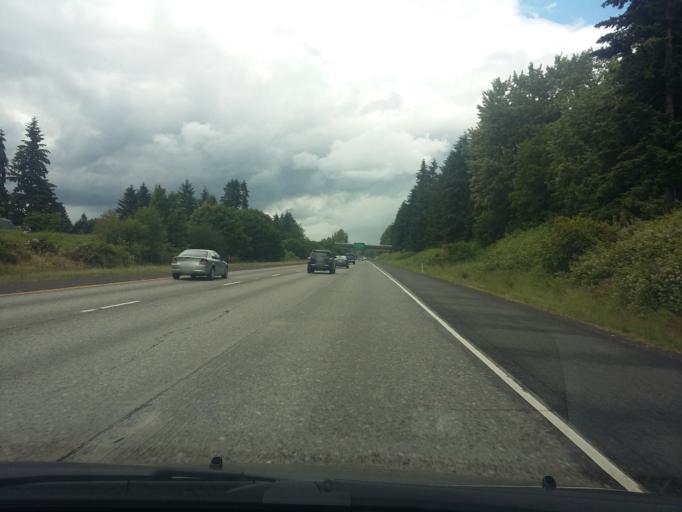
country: US
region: Washington
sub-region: Clark County
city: Orchards
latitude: 45.6653
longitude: -122.5779
